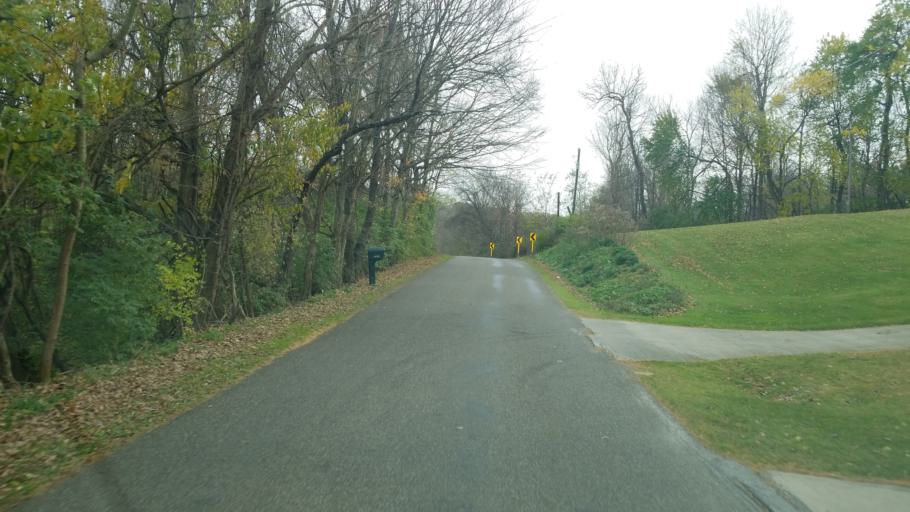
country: US
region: Ohio
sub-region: Richland County
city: Mansfield
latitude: 40.7220
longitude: -82.4953
